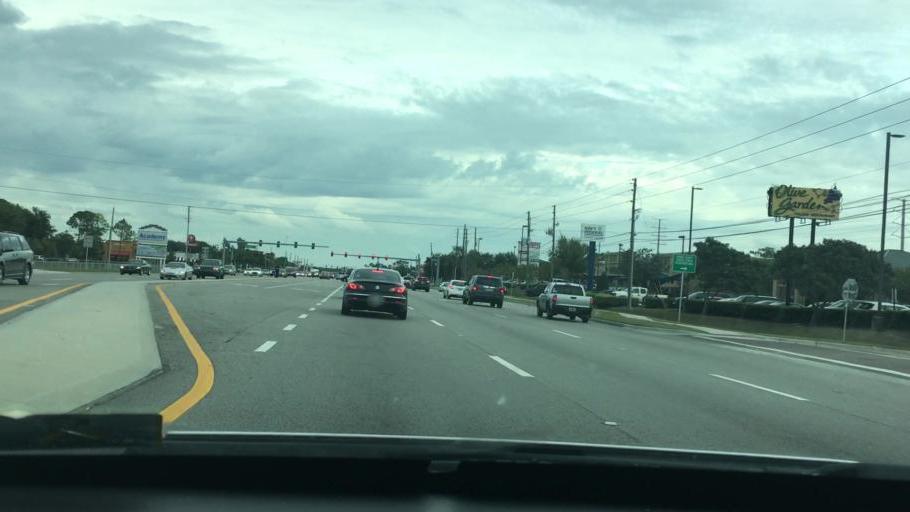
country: US
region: Florida
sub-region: Orange County
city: Alafaya
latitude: 28.5665
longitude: -81.2057
